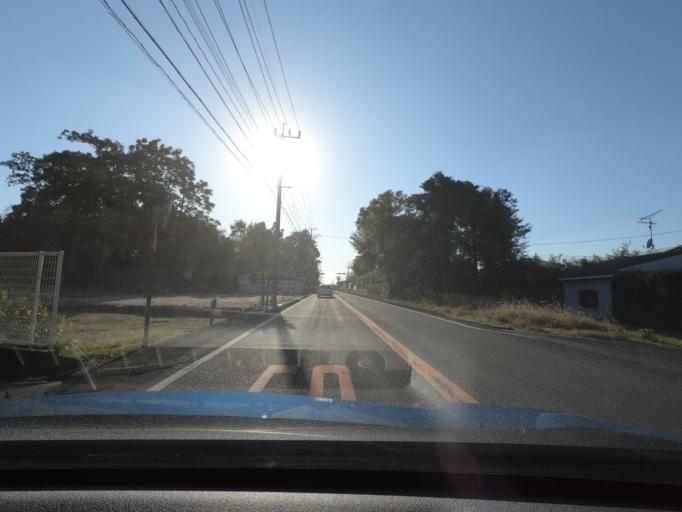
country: JP
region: Kagoshima
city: Izumi
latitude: 32.0860
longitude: 130.2814
